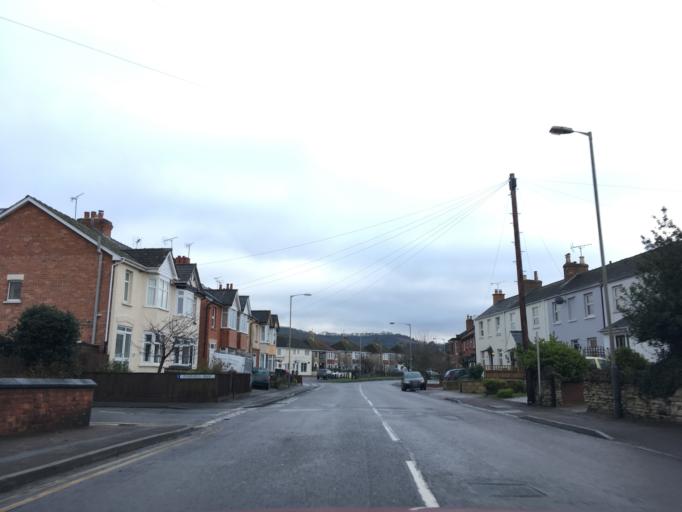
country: GB
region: England
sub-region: Gloucestershire
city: Charlton Kings
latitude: 51.8806
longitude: -2.0550
